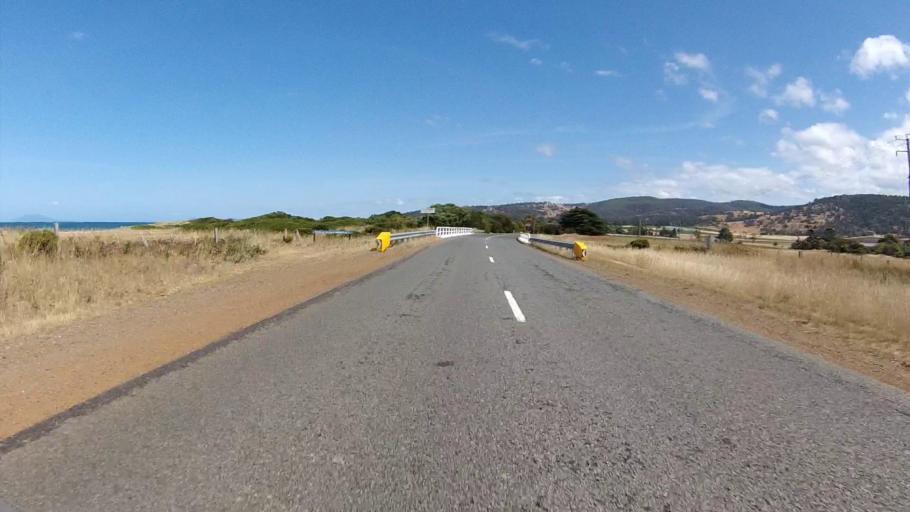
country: AU
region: Tasmania
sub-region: Sorell
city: Sorell
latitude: -42.1978
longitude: 148.0502
